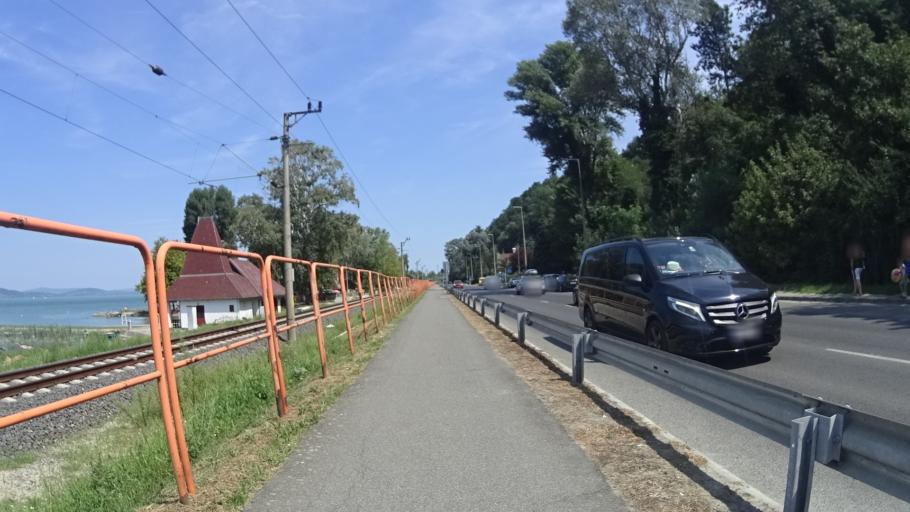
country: HU
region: Somogy
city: Fonyod
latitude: 46.7442
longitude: 17.5431
